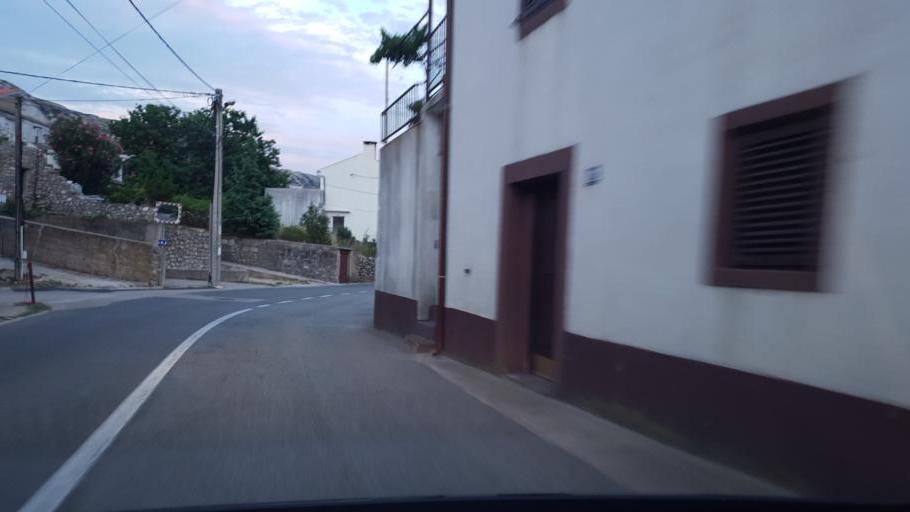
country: HR
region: Primorsko-Goranska
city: Punat
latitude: 44.9989
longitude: 14.7111
